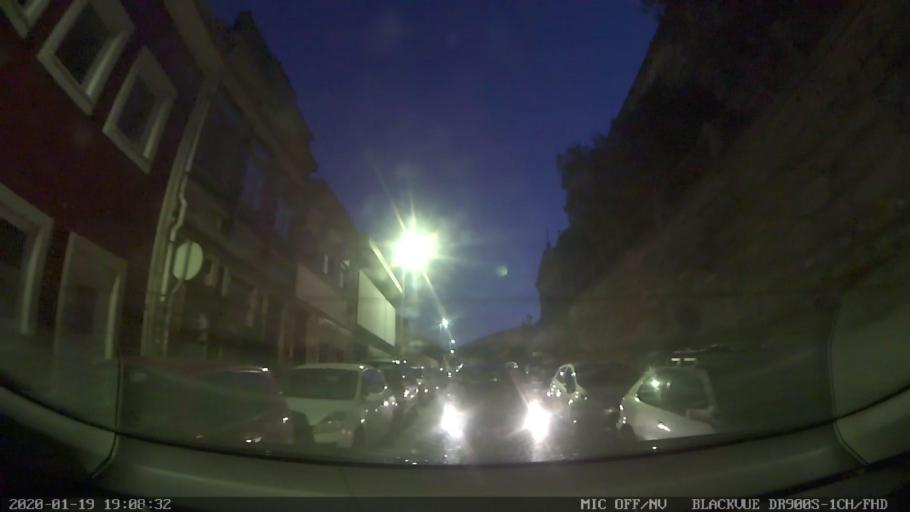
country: PT
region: Porto
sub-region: Porto
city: Porto
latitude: 41.1506
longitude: -8.6280
